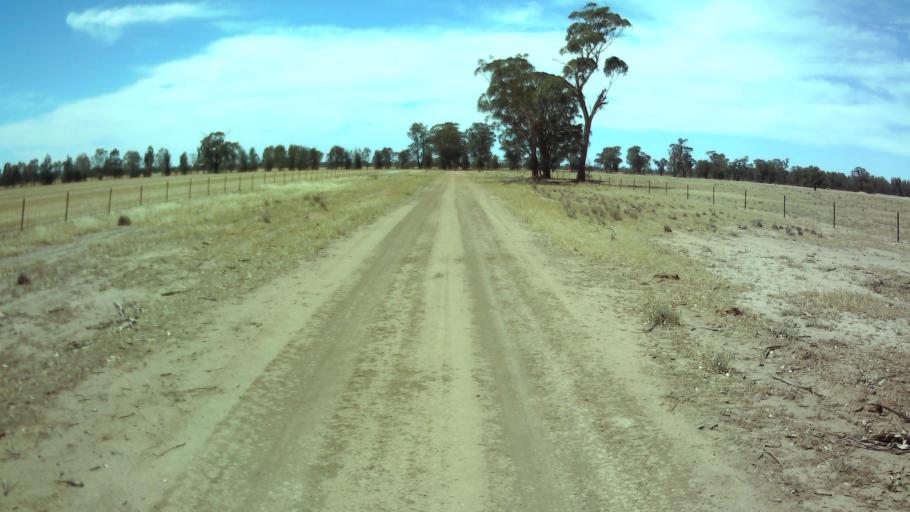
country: AU
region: New South Wales
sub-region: Weddin
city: Grenfell
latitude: -33.9013
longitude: 147.8057
